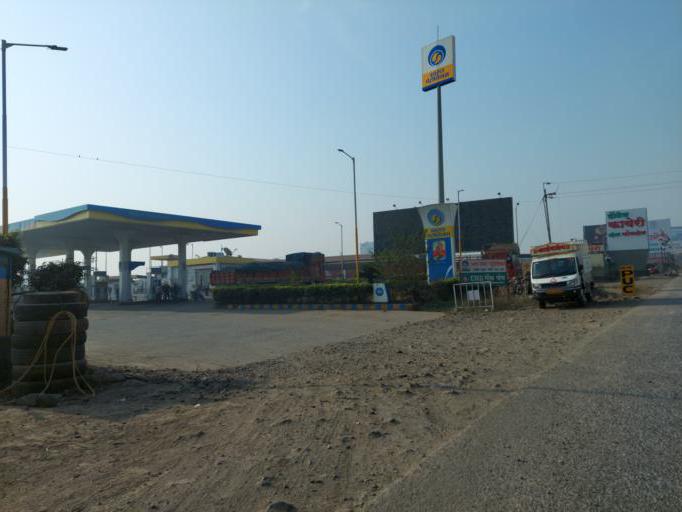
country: IN
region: Maharashtra
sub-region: Pune Division
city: Pune
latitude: 18.4623
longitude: 73.9511
